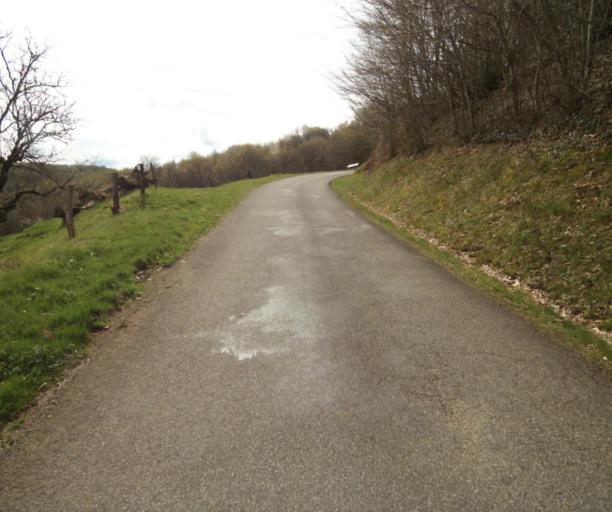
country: FR
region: Limousin
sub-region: Departement de la Correze
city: Laguenne
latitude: 45.2420
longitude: 1.8422
